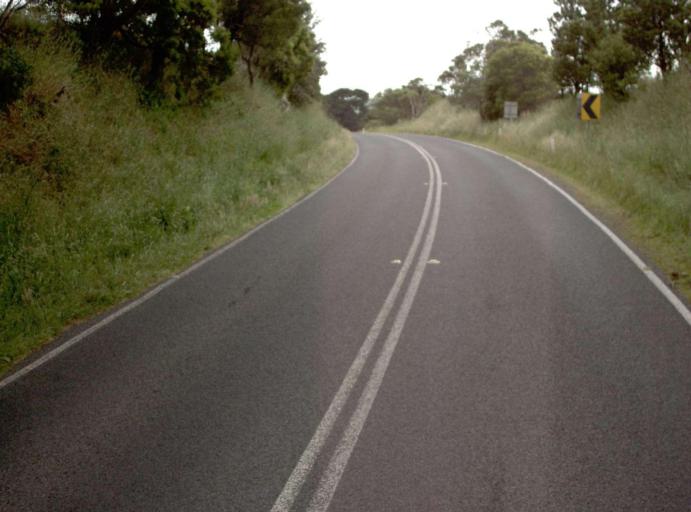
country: AU
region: Victoria
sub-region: Bass Coast
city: North Wonthaggi
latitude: -38.4766
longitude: 145.7659
